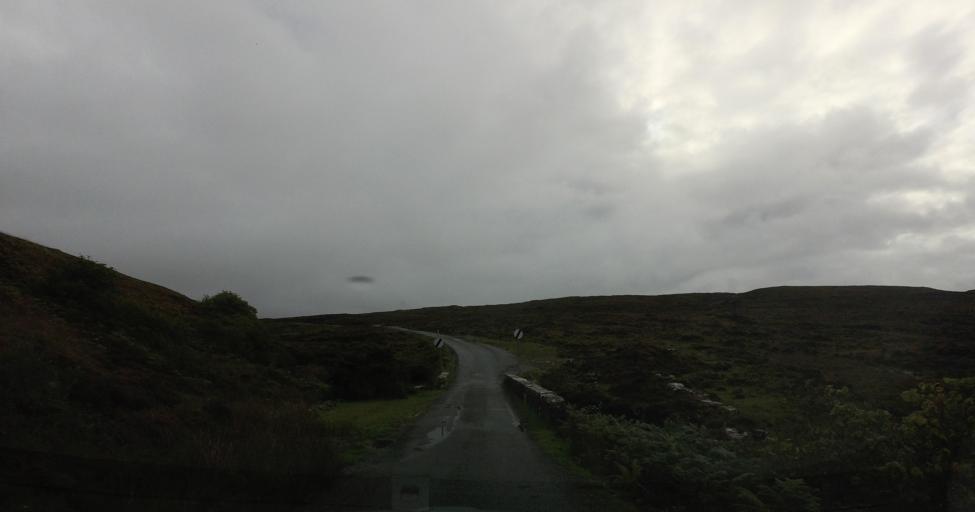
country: GB
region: Scotland
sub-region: Highland
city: Isle of Skye
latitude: 57.1453
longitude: -6.1012
